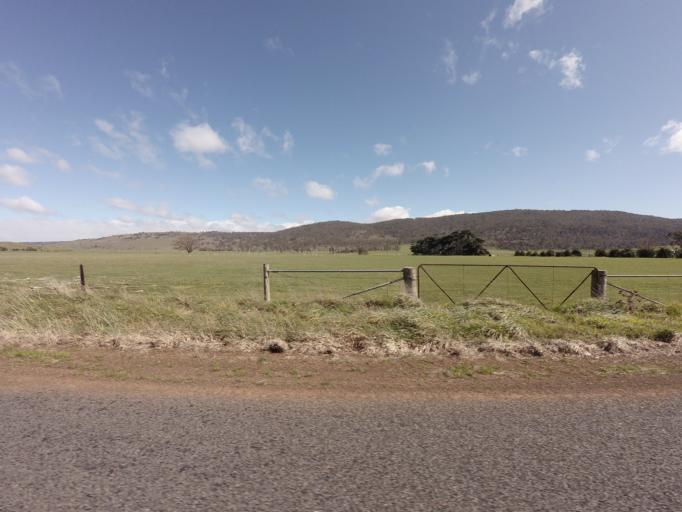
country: AU
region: Tasmania
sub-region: Northern Midlands
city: Evandale
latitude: -41.9842
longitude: 147.4500
